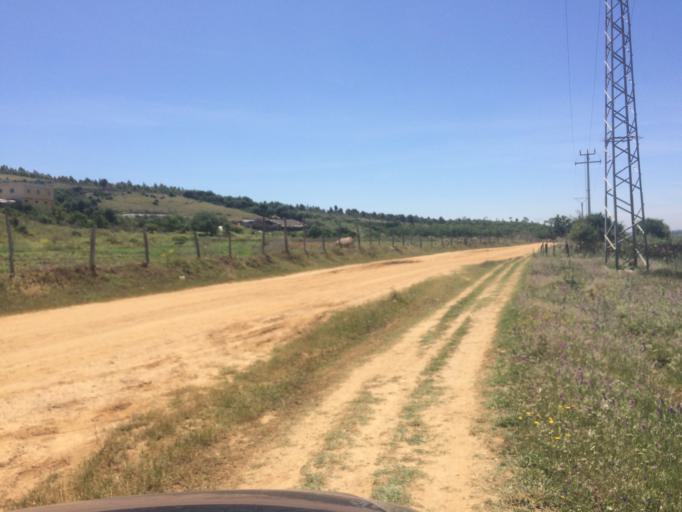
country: MA
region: Tanger-Tetouan
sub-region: Larache
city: Larache
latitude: 35.1898
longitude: -6.0811
